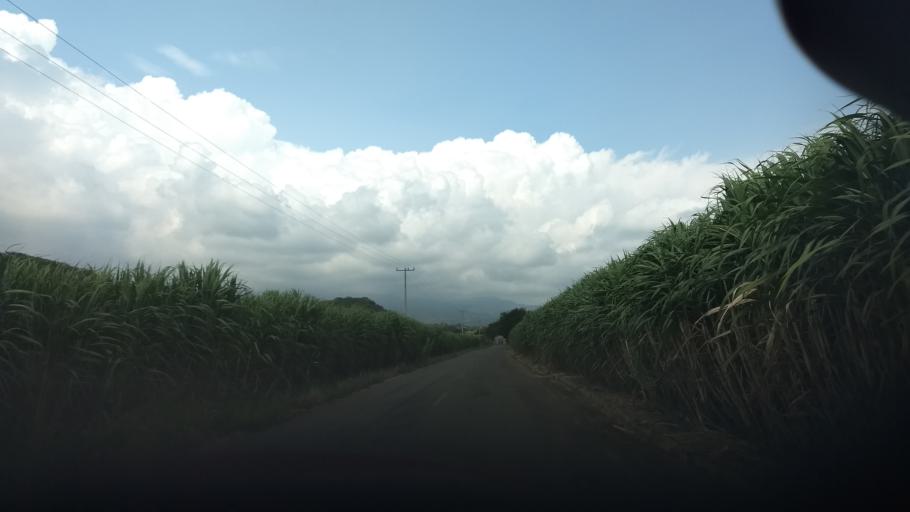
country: MX
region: Jalisco
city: Tonila
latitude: 19.4186
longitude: -103.4890
